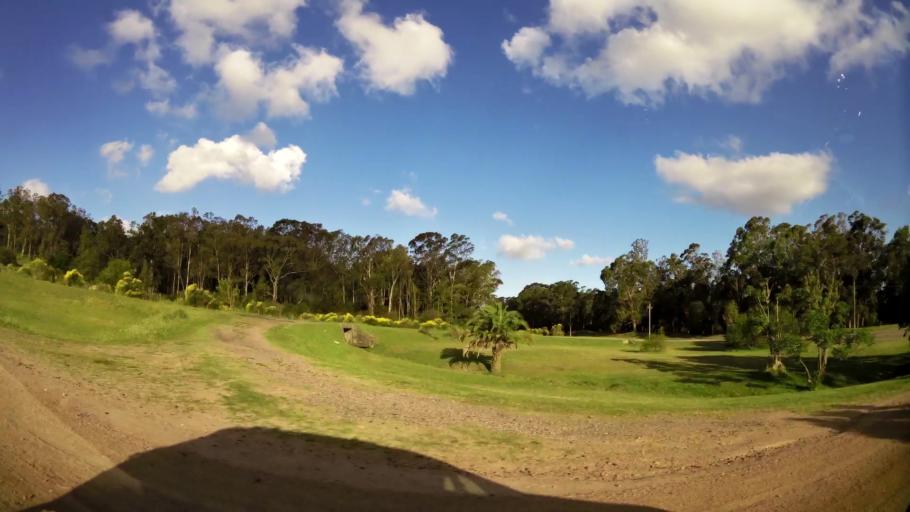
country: UY
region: Montevideo
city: Montevideo
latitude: -34.8948
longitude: -56.2611
